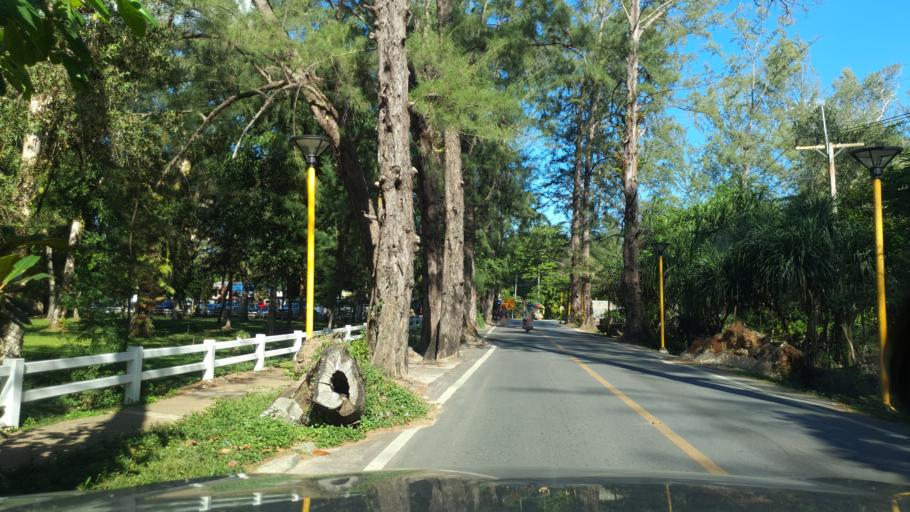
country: TH
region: Phangnga
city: Ban Ao Nang
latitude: 8.0467
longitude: 98.8019
